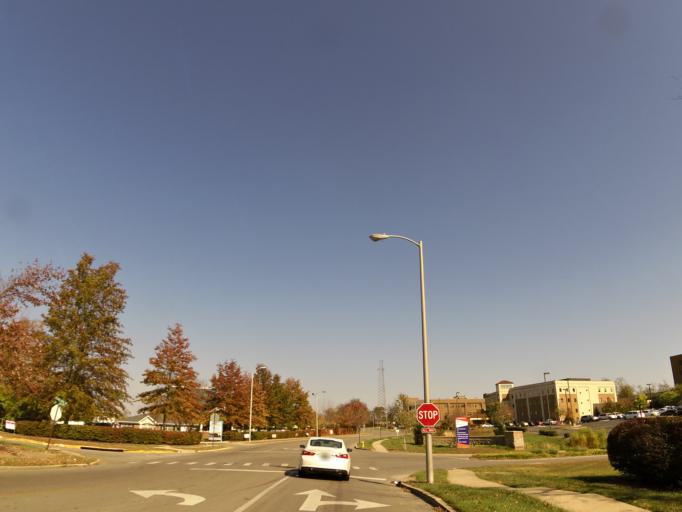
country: US
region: Kentucky
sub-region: Fayette County
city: Lexington
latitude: 37.9992
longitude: -84.4416
